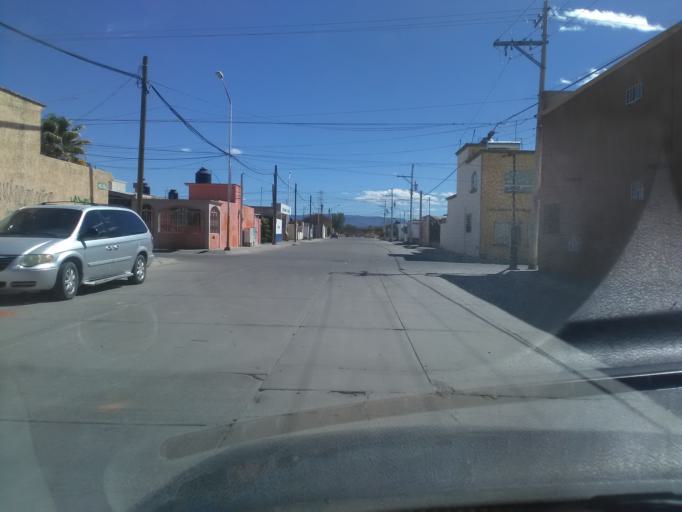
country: MX
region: Durango
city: Victoria de Durango
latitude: 24.0049
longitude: -104.6286
